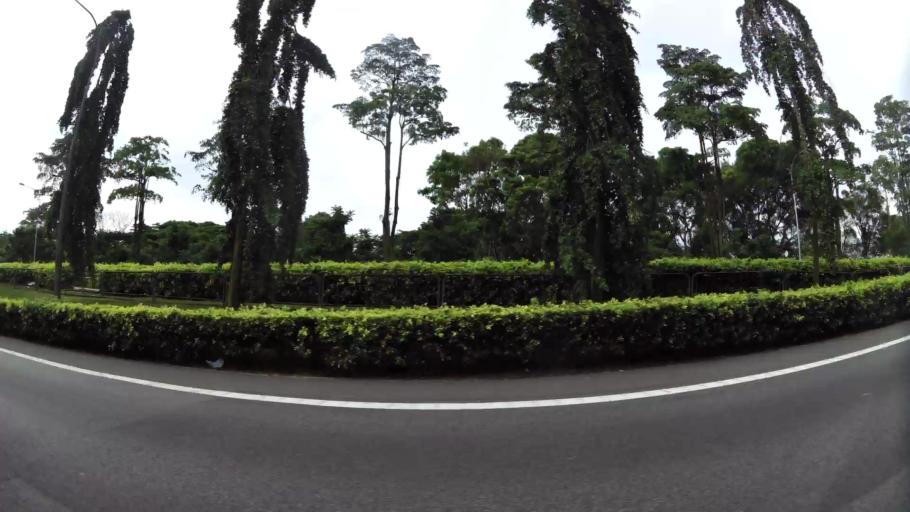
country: MY
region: Johor
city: Johor Bahru
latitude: 1.3672
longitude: 103.7109
